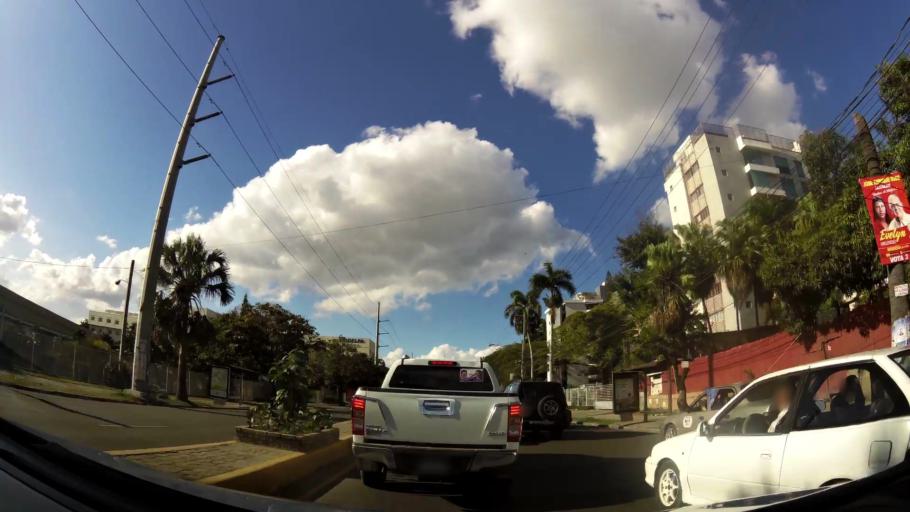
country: DO
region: Santiago
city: Santiago de los Caballeros
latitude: 19.4642
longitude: -70.6865
